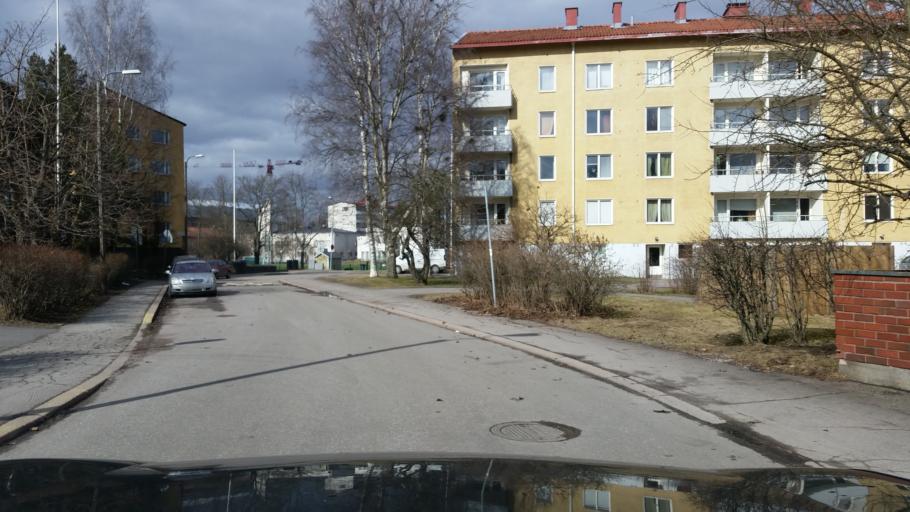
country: FI
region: Uusimaa
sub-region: Helsinki
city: Teekkarikylae
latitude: 60.1949
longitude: 24.8761
